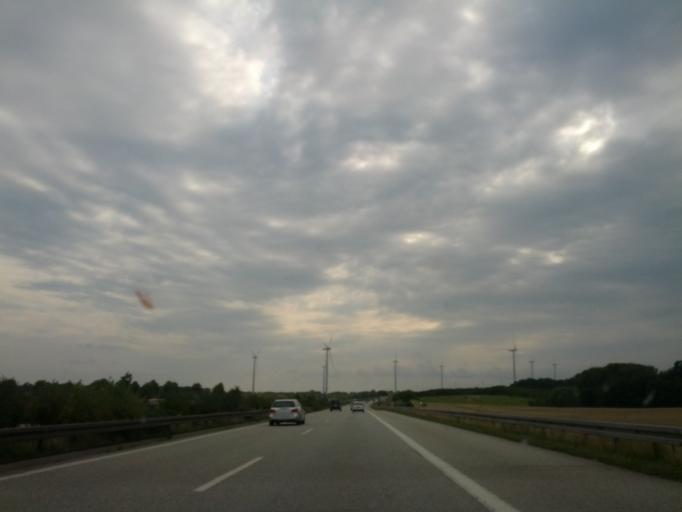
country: DE
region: Mecklenburg-Vorpommern
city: Jurgenshagen
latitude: 53.9775
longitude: 11.9147
